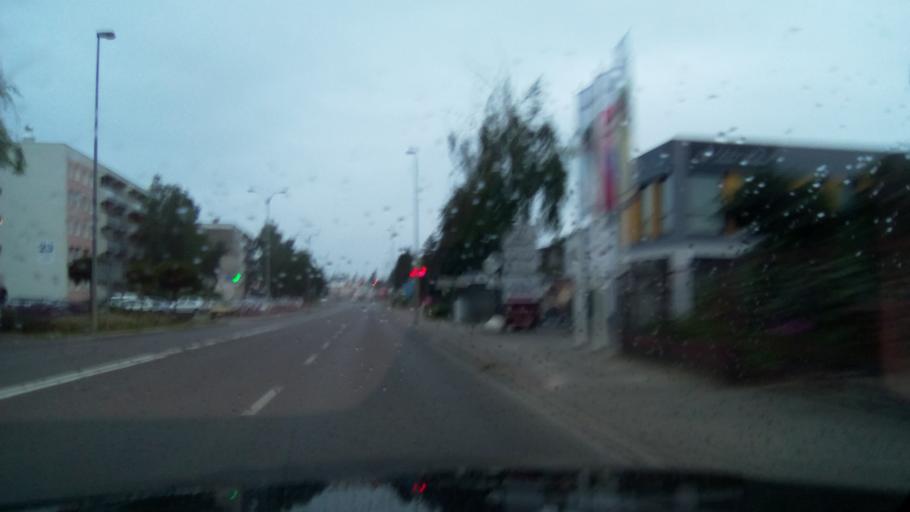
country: PL
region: Greater Poland Voivodeship
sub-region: Powiat poznanski
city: Swarzedz
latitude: 52.4136
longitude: 17.0854
